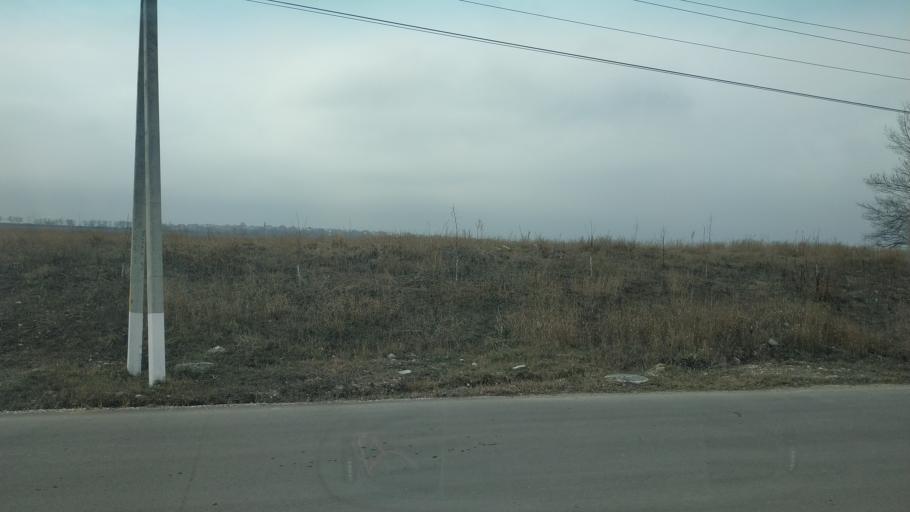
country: MD
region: Chisinau
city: Singera
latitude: 46.9100
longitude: 29.0071
